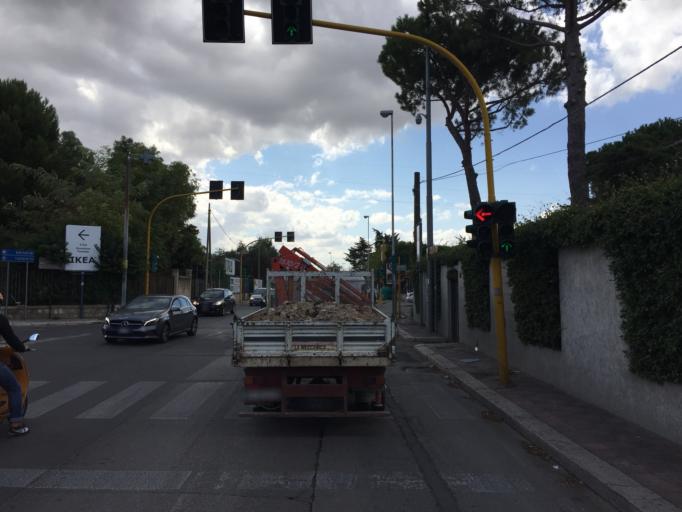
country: IT
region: Apulia
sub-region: Provincia di Bari
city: Bari
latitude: 41.0940
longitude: 16.8833
